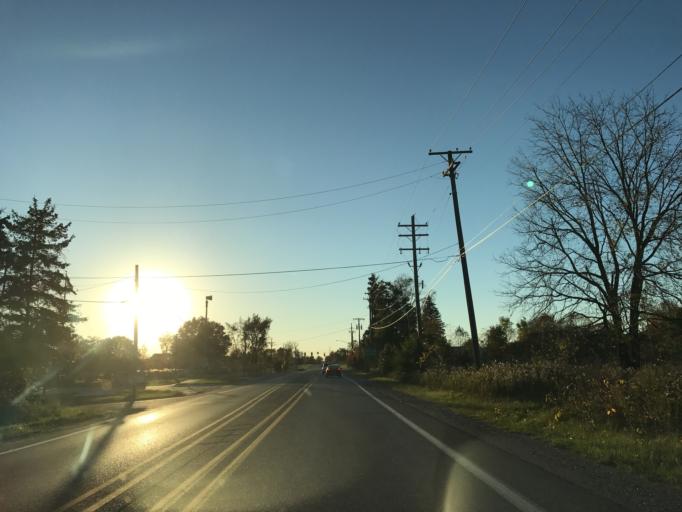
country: US
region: Michigan
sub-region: Oakland County
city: South Lyon
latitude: 42.4621
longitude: -83.6092
